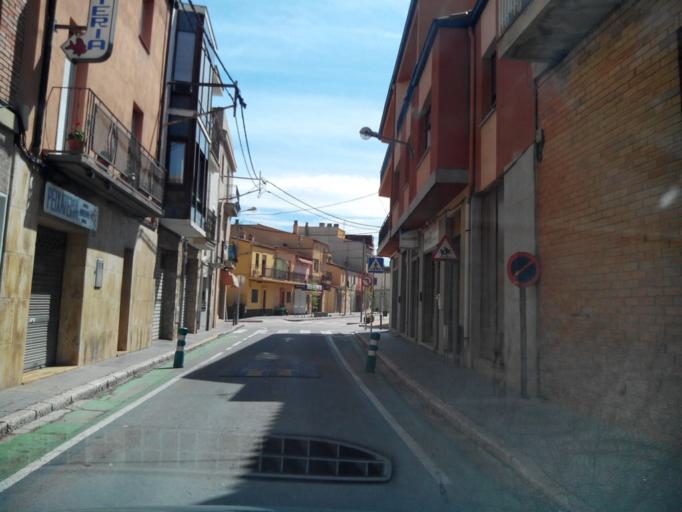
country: ES
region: Catalonia
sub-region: Provincia de Girona
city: Sant Pere Pescador
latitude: 42.1886
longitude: 3.0823
